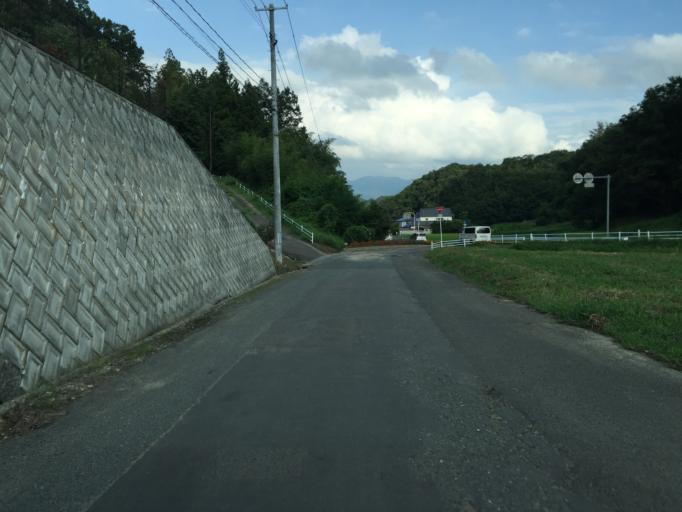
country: JP
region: Fukushima
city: Fukushima-shi
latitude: 37.6830
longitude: 140.5548
